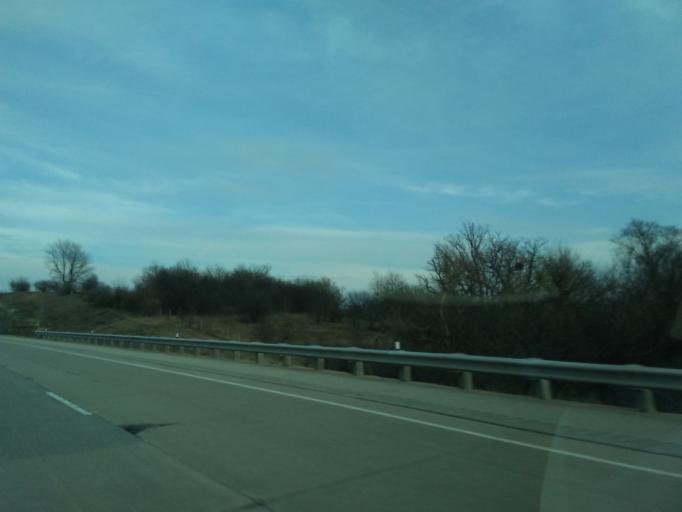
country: US
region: Wisconsin
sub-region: Dane County
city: Mount Horeb
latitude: 42.9926
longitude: -89.7357
